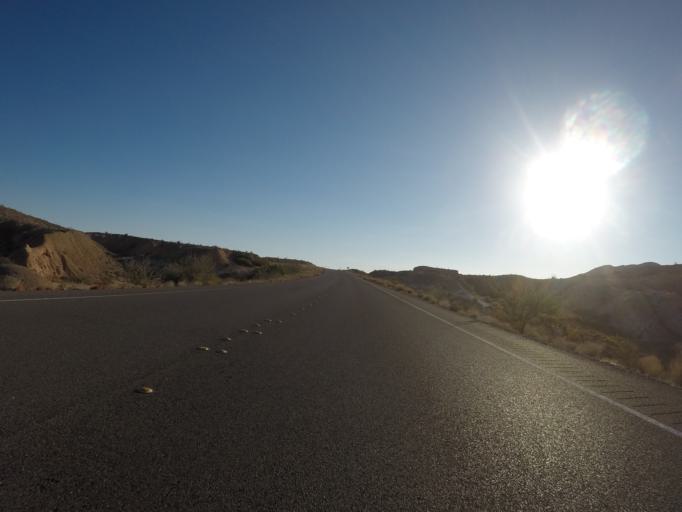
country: US
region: Nevada
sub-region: Clark County
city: Moapa Valley
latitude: 36.3972
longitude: -114.4238
